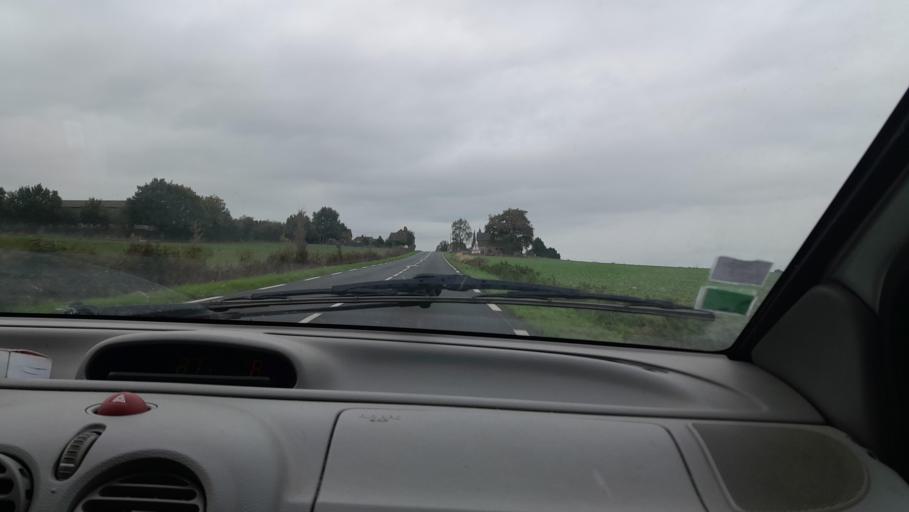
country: FR
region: Pays de la Loire
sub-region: Departement de la Loire-Atlantique
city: Saint-Mars-la-Jaille
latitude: 47.5795
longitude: -1.1910
